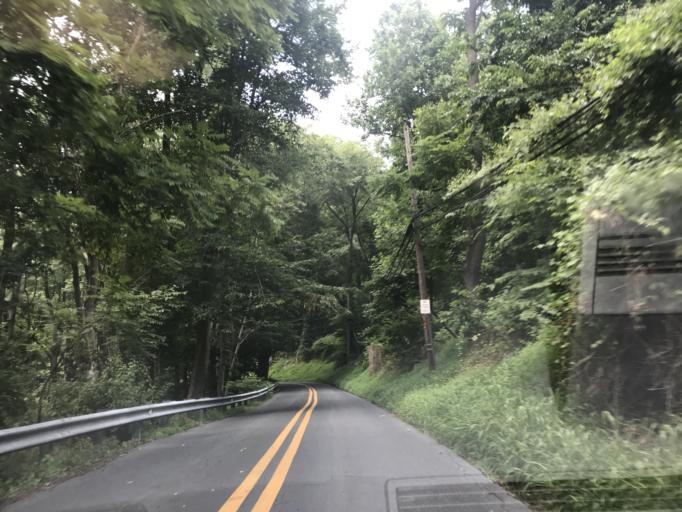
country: US
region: Delaware
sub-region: New Castle County
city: Greenville
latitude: 39.7634
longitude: -75.6358
